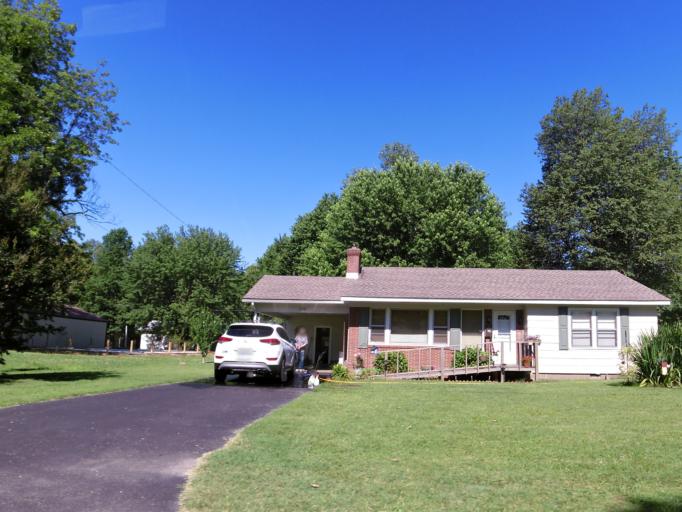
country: US
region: Arkansas
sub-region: Clay County
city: Piggott
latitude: 36.3891
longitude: -90.1941
